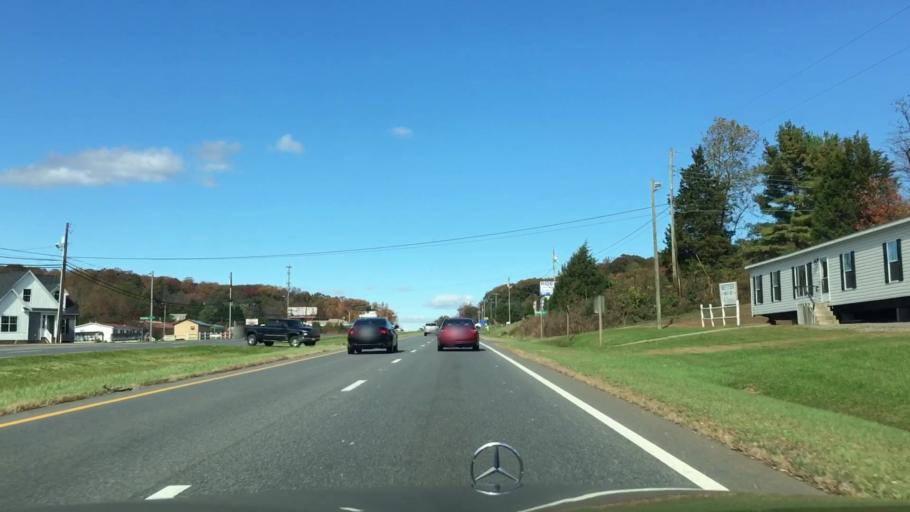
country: US
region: Virginia
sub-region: Campbell County
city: Rustburg
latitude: 37.2929
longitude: -79.1699
